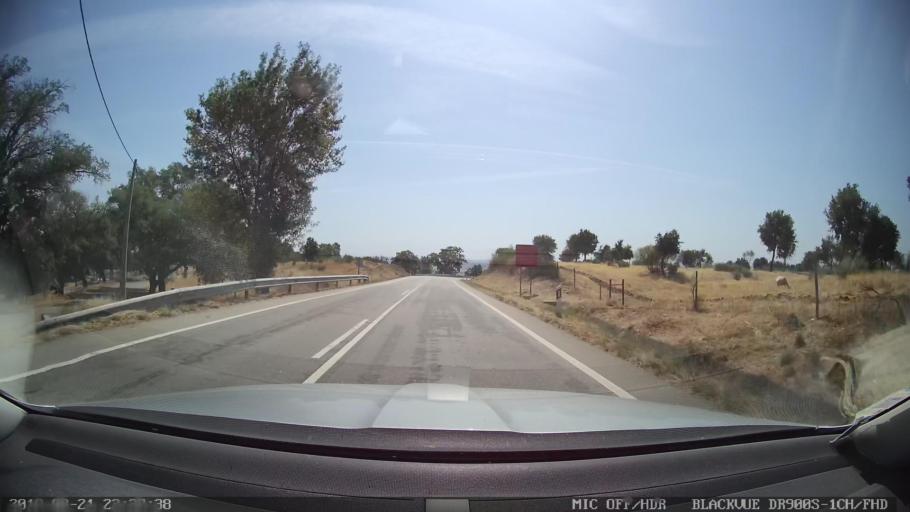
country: PT
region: Guarda
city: Alcains
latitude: 39.8669
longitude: -7.3578
